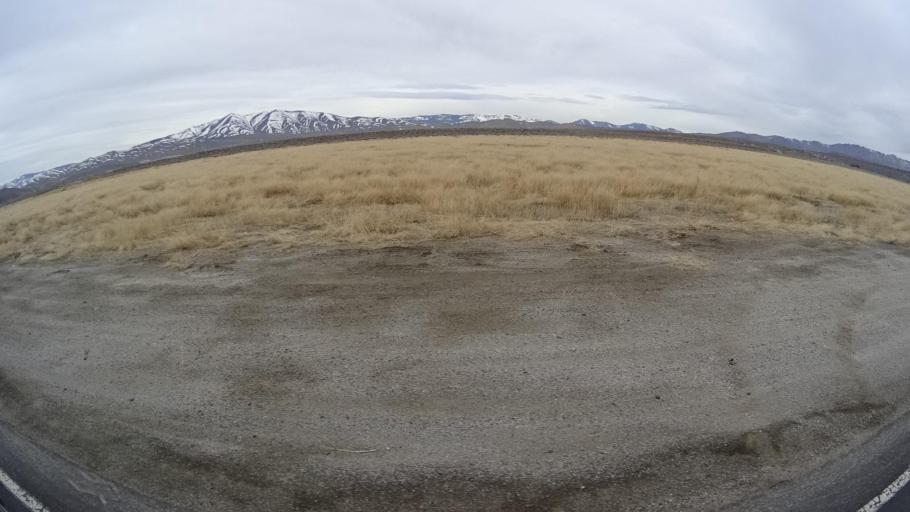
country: US
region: Nevada
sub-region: Washoe County
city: Lemmon Valley
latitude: 39.6621
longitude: -119.8287
